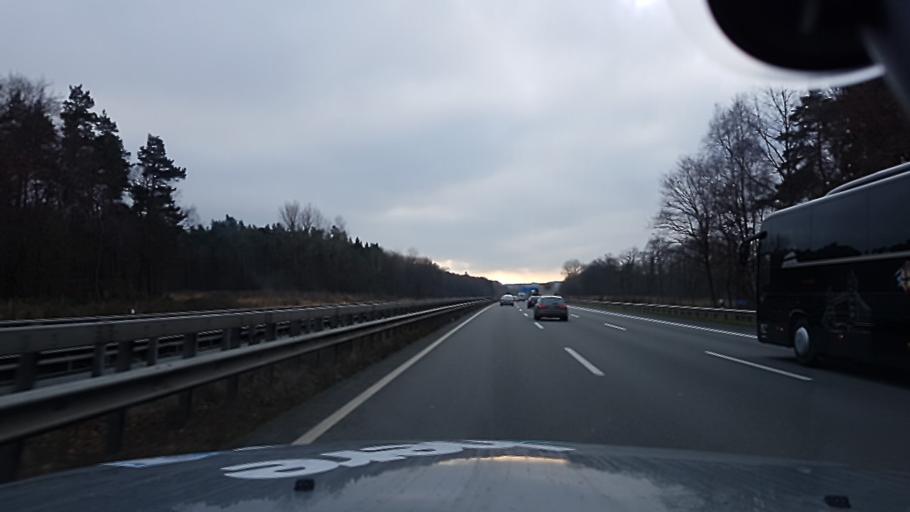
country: DE
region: Lower Saxony
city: Wallenhorst
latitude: 52.3588
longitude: 8.0378
